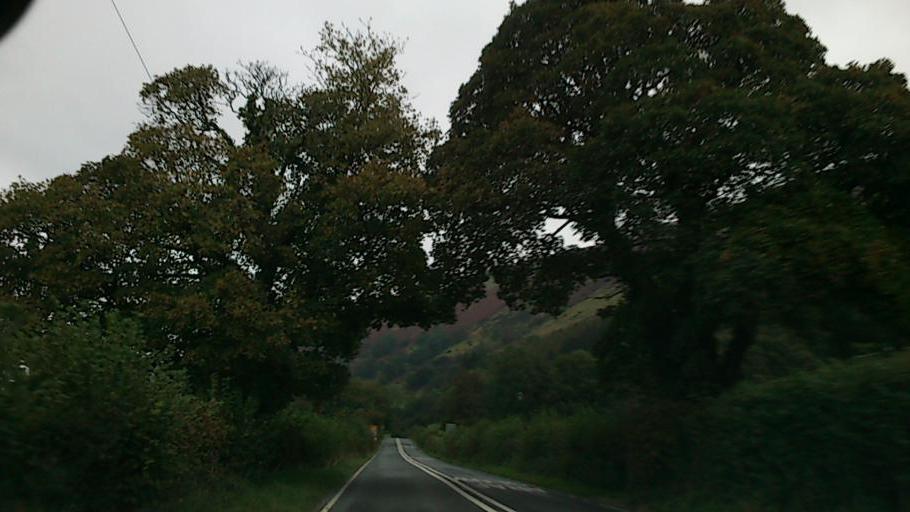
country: GB
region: Wales
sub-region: Gwynedd
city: Corris
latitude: 52.6860
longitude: -3.6901
